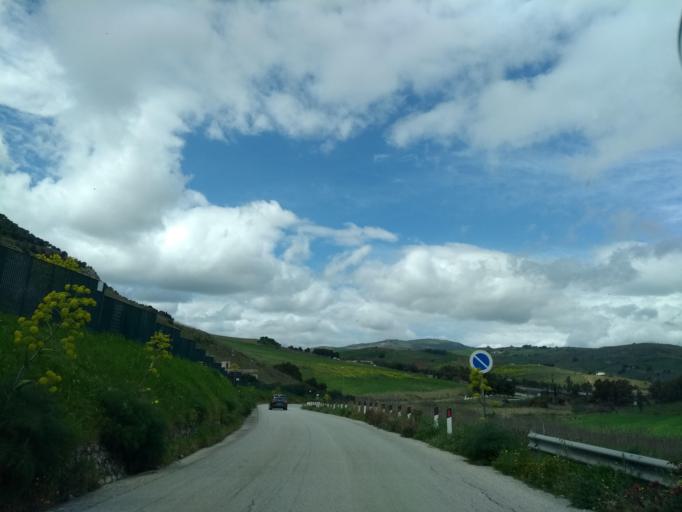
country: IT
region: Sicily
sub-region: Trapani
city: Calatafimi
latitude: 37.9429
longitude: 12.8357
